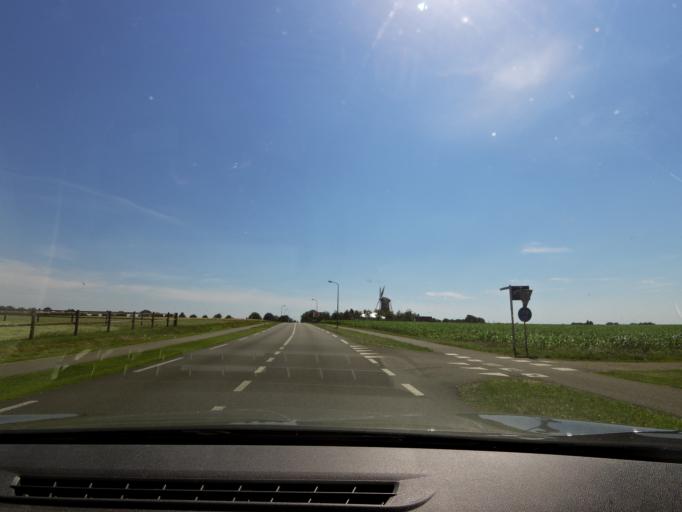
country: NL
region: Gelderland
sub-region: Berkelland
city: Neede
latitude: 52.1440
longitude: 6.6110
